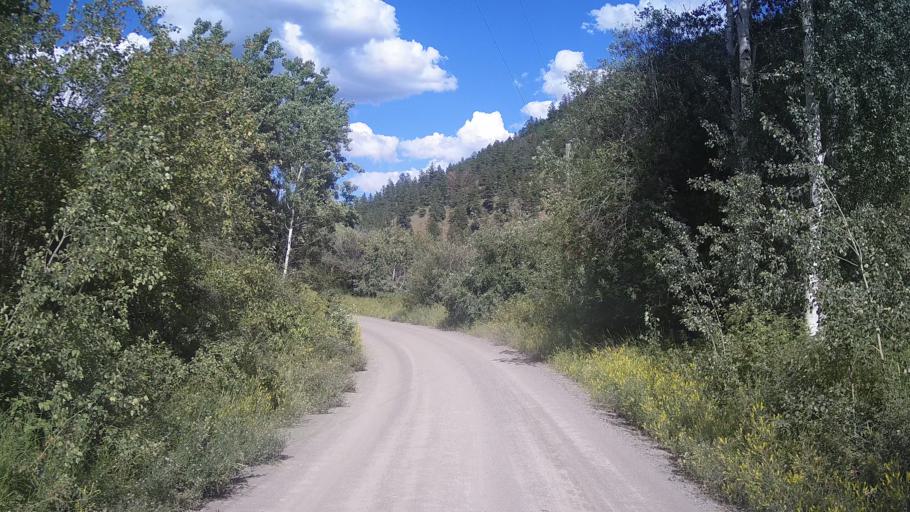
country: CA
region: British Columbia
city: Lillooet
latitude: 51.2421
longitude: -122.0406
